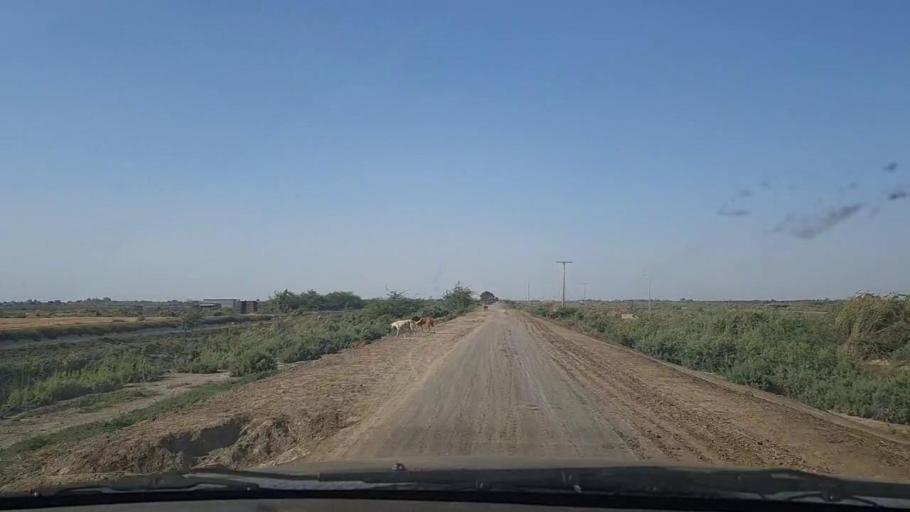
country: PK
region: Sindh
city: Chuhar Jamali
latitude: 24.3061
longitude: 67.7548
